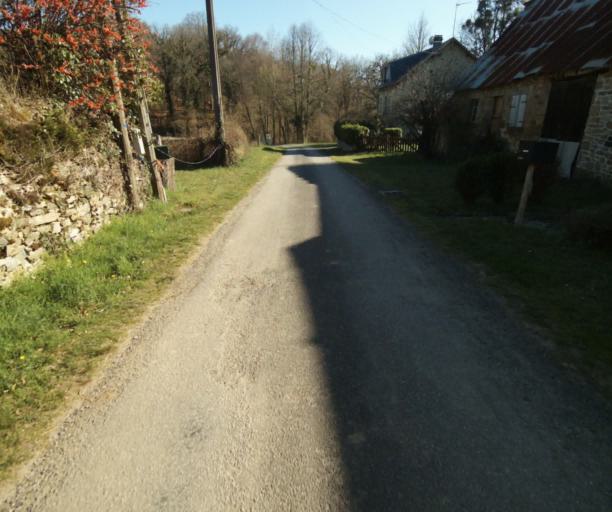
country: FR
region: Limousin
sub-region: Departement de la Correze
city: Chamboulive
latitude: 45.4824
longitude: 1.7001
